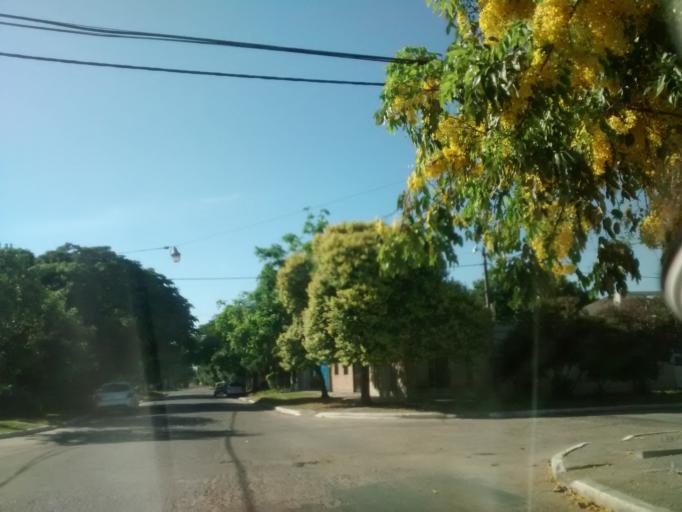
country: AR
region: Chaco
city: Resistencia
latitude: -27.4424
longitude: -59.0033
